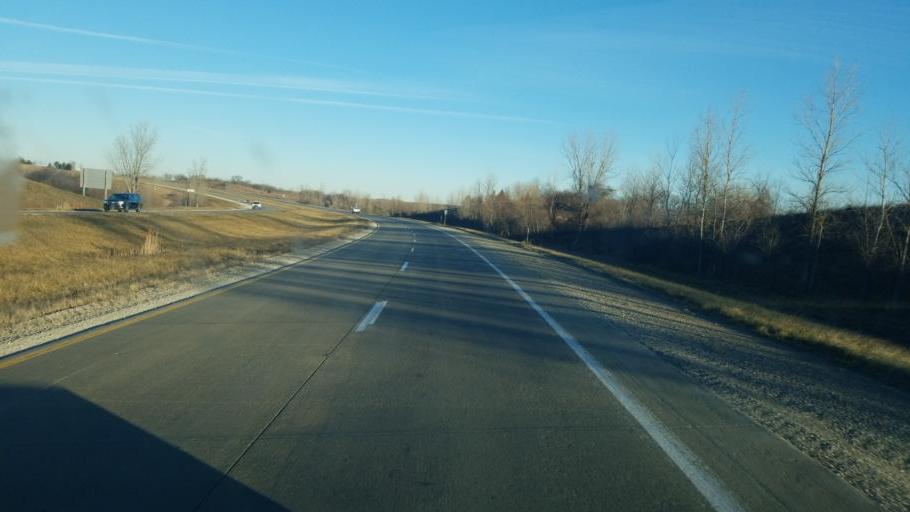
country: US
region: Iowa
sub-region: Mahaska County
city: Oskaloosa
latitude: 41.3038
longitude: -92.6747
